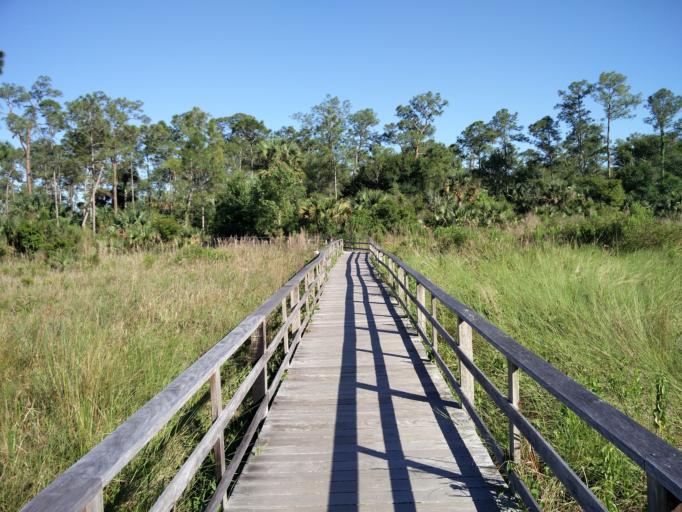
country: US
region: Florida
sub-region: Collier County
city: Orangetree
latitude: 26.3765
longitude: -81.6063
